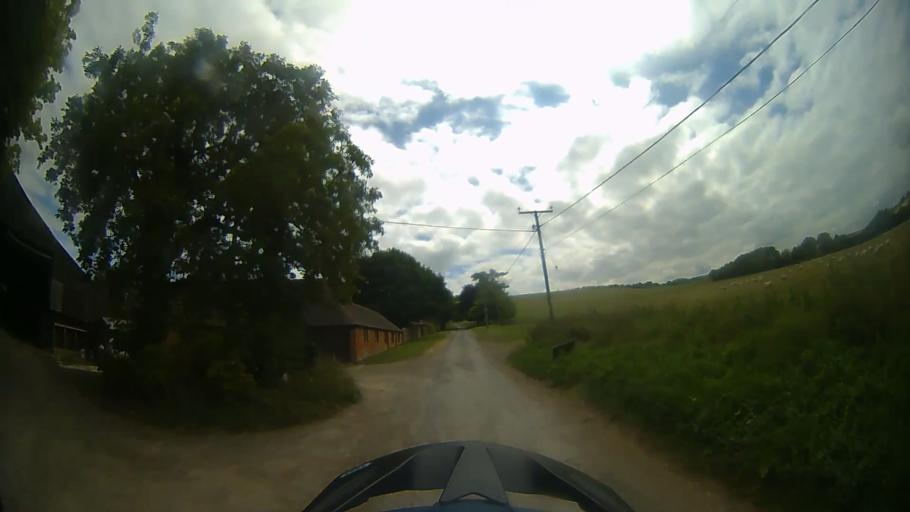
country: GB
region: England
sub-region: Oxfordshire
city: Wantage
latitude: 51.5660
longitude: -1.4467
